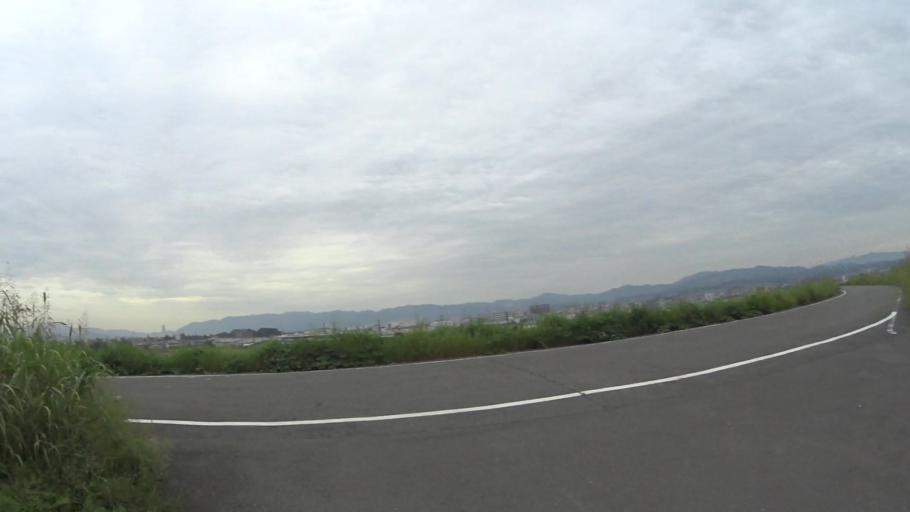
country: JP
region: Kyoto
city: Uji
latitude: 34.8640
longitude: 135.7769
